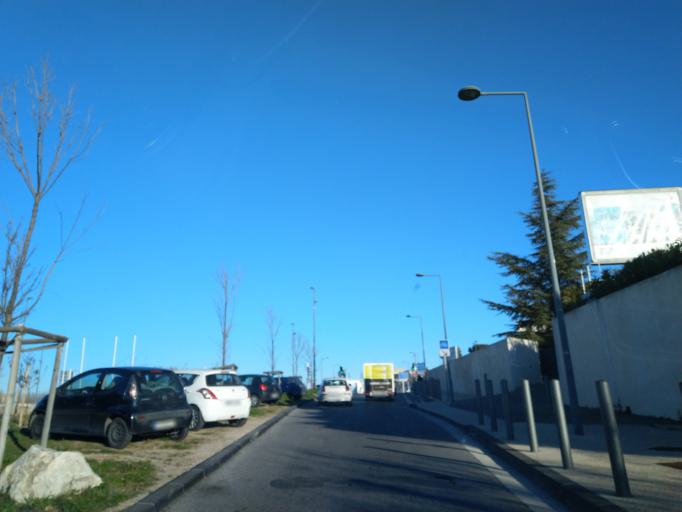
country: FR
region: Provence-Alpes-Cote d'Azur
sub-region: Departement des Bouches-du-Rhone
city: Marseille 12
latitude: 43.3069
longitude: 5.4255
